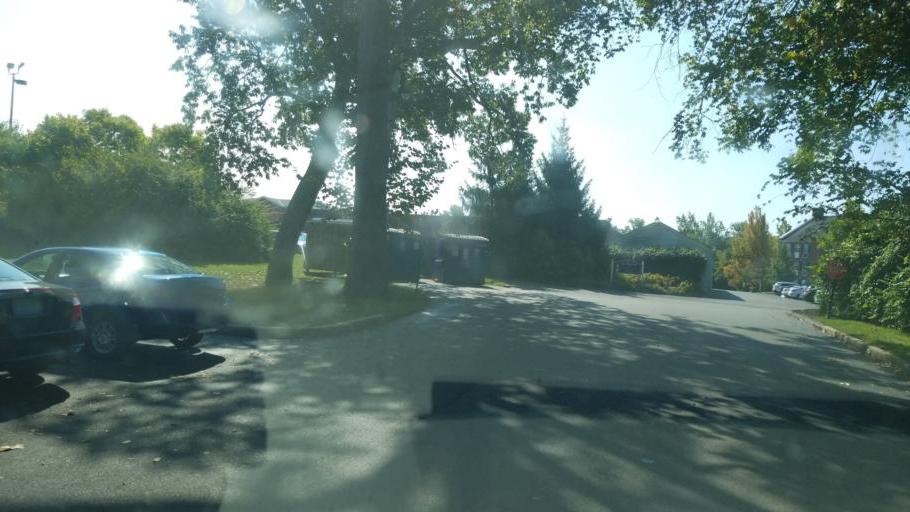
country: US
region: Ohio
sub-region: Franklin County
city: Grandview Heights
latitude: 40.0202
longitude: -83.0145
